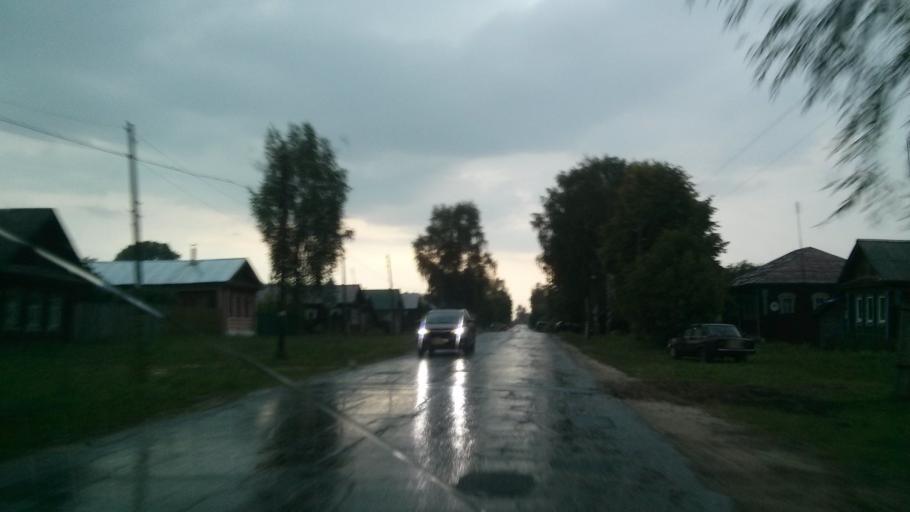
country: RU
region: Nizjnij Novgorod
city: Shimorskoye
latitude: 55.3510
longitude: 41.9316
